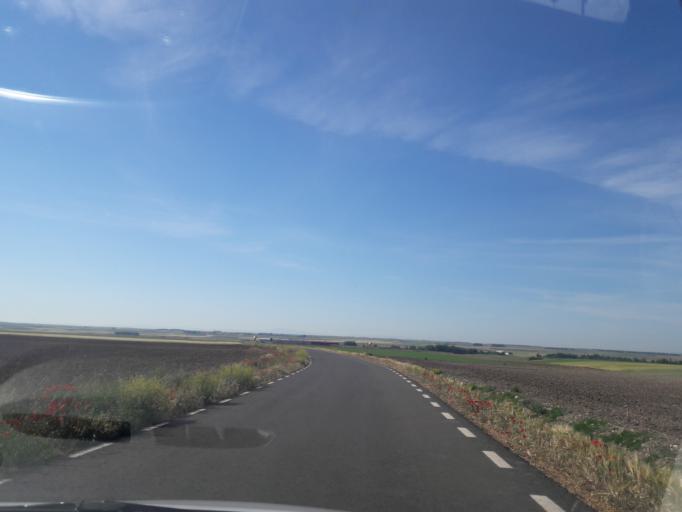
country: ES
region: Castille and Leon
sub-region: Provincia de Salamanca
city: Espino de la Orbada
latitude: 41.1213
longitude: -5.4287
